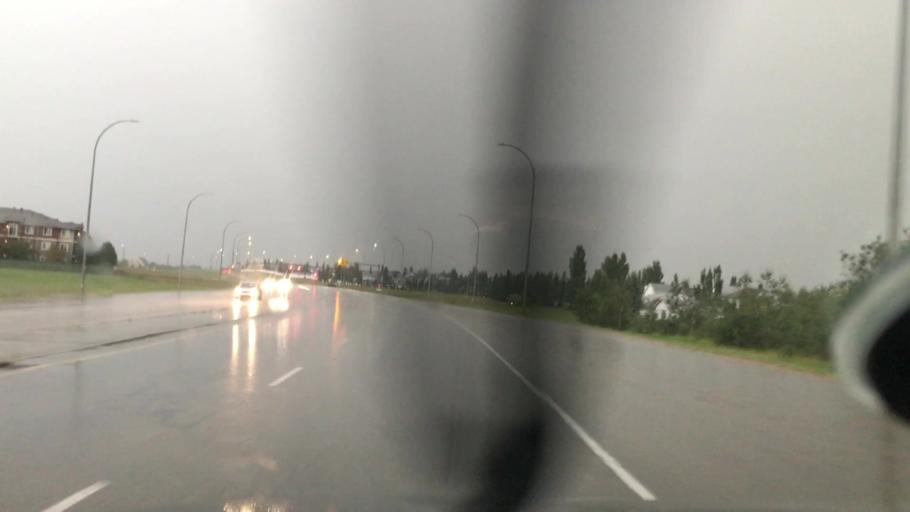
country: CA
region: Alberta
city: Edmonton
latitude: 53.4484
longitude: -113.5911
